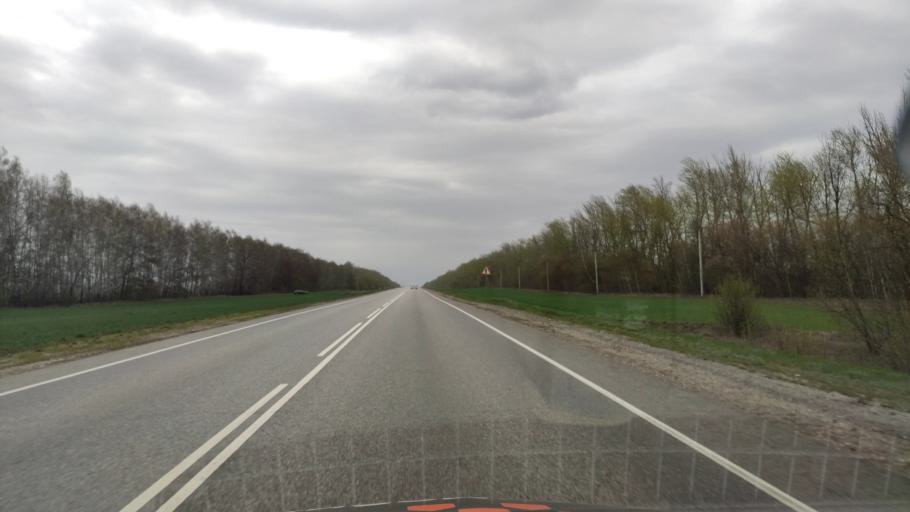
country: RU
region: Kursk
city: Gorshechnoye
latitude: 51.5493
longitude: 38.1524
